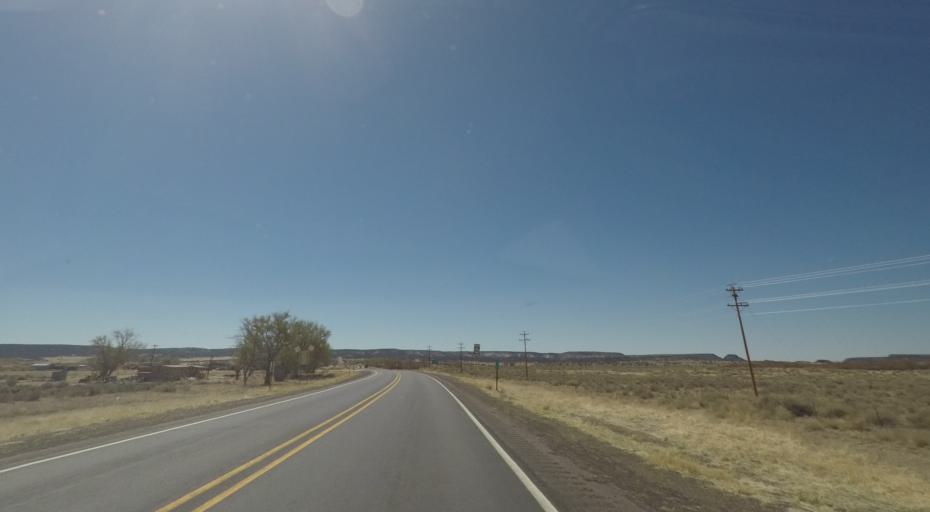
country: US
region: New Mexico
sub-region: Catron County
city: Reserve
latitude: 34.3443
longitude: -108.5027
